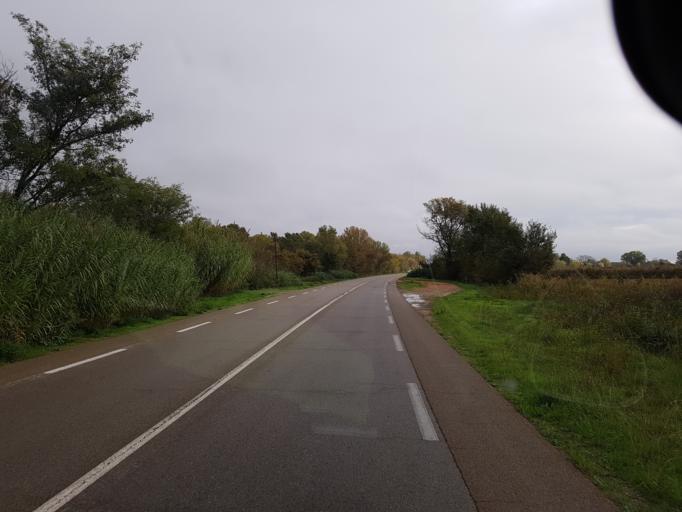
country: FR
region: Languedoc-Roussillon
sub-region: Departement du Gard
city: Saint-Gilles
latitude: 43.6681
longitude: 4.4703
